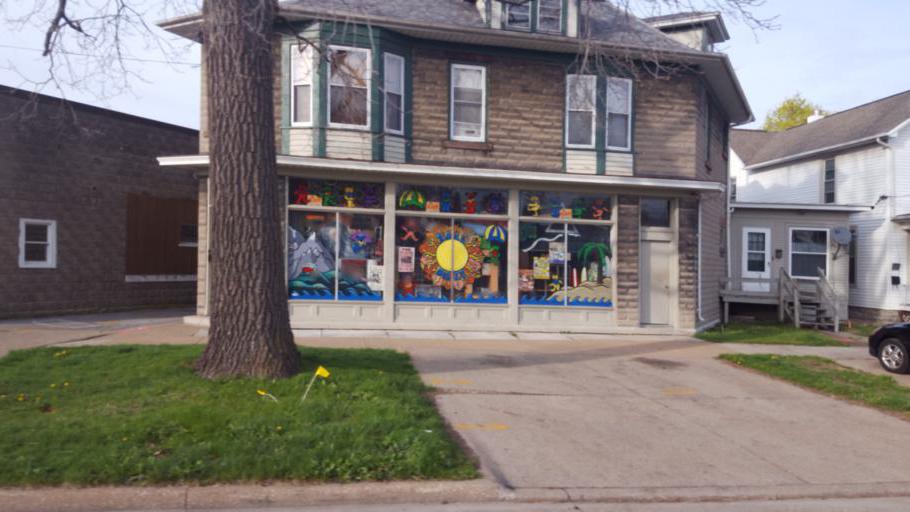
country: US
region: Ohio
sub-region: Erie County
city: Sandusky
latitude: 41.4540
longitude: -82.7064
